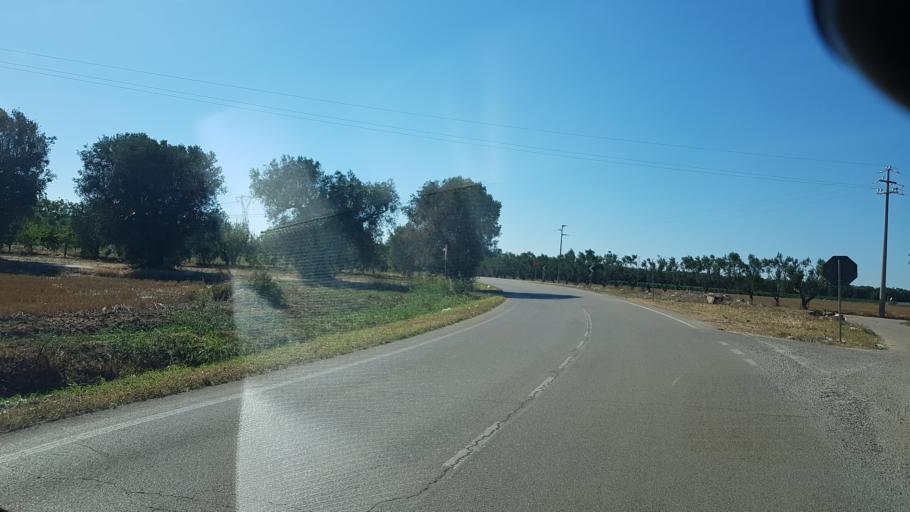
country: IT
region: Apulia
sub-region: Provincia di Brindisi
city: Mesagne
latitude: 40.5554
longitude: 17.8645
